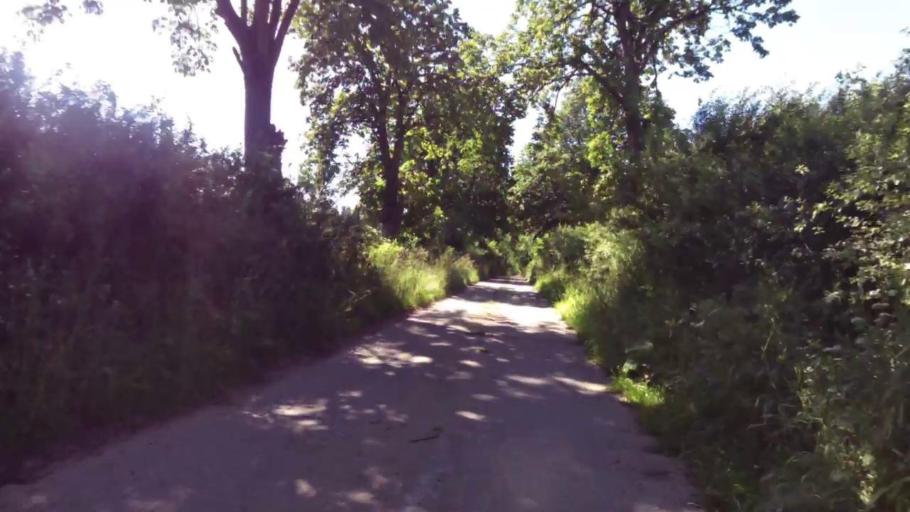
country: PL
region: West Pomeranian Voivodeship
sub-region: Powiat bialogardzki
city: Bialogard
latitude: 53.9277
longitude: 16.0077
